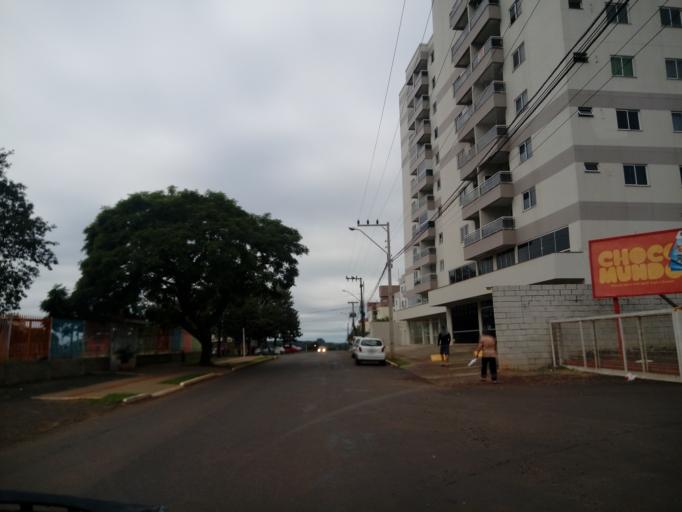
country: BR
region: Santa Catarina
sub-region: Chapeco
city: Chapeco
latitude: -27.0964
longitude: -52.6376
